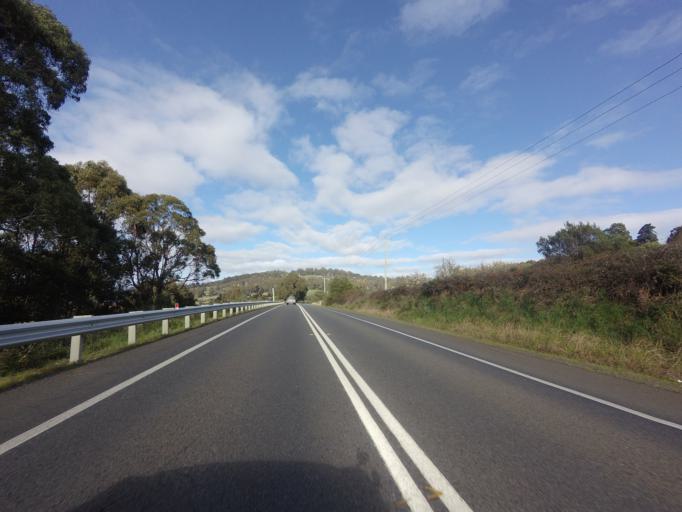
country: AU
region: Tasmania
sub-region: Huon Valley
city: Franklin
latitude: -43.1109
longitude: 146.9982
